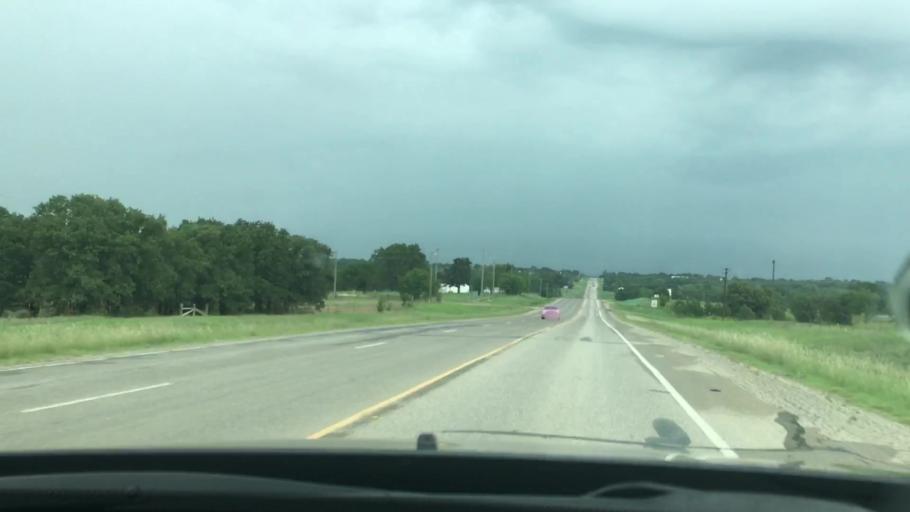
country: US
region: Oklahoma
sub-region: Carter County
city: Healdton
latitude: 34.2001
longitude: -97.4747
